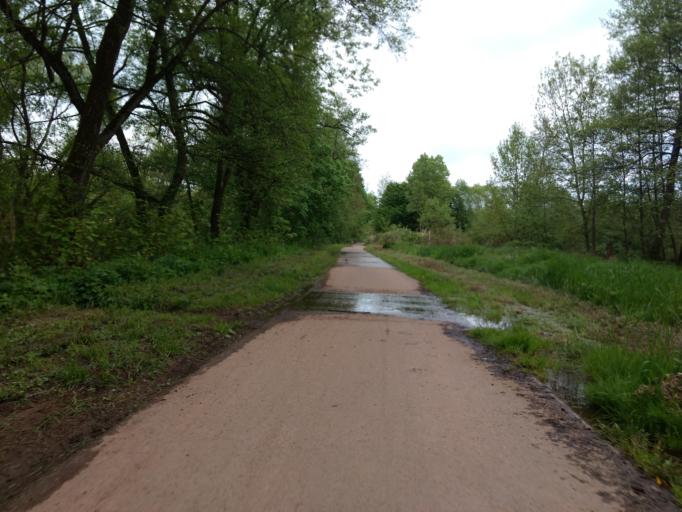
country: DE
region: Saarland
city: Nalbach
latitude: 49.3824
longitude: 6.8079
